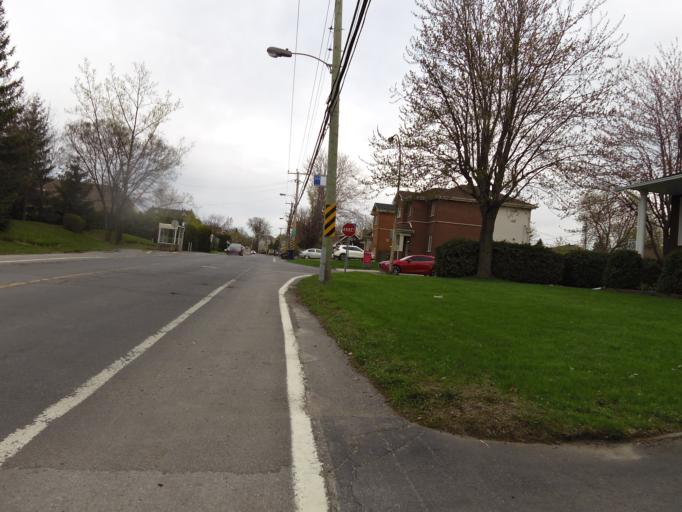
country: CA
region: Quebec
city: Dollard-Des Ormeaux
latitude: 45.5184
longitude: -73.7978
